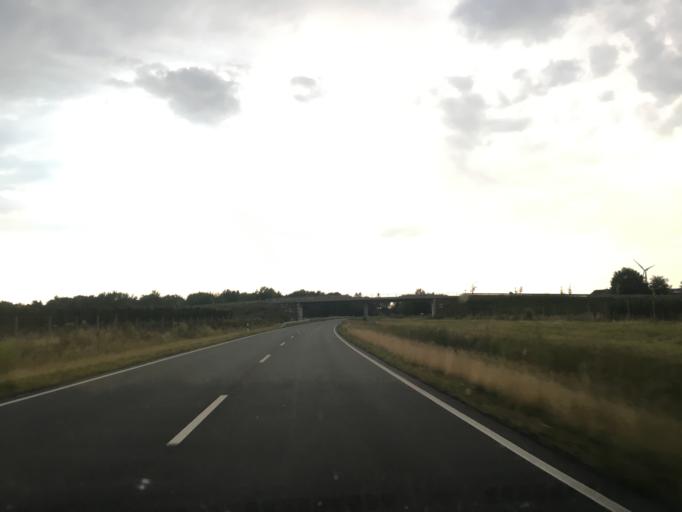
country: DE
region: North Rhine-Westphalia
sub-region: Regierungsbezirk Munster
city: Telgte
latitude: 51.9260
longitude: 7.7137
